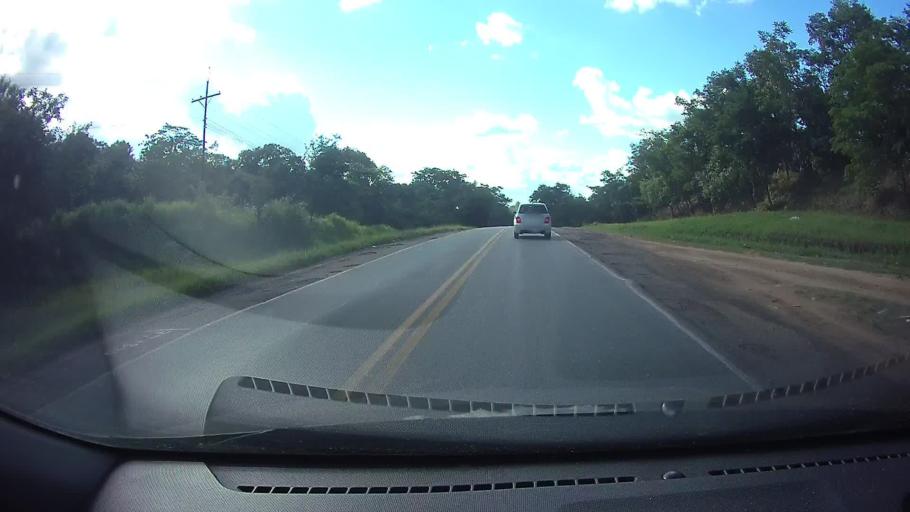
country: PY
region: Cordillera
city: Eusebio Ayala
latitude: -25.4159
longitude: -56.9308
